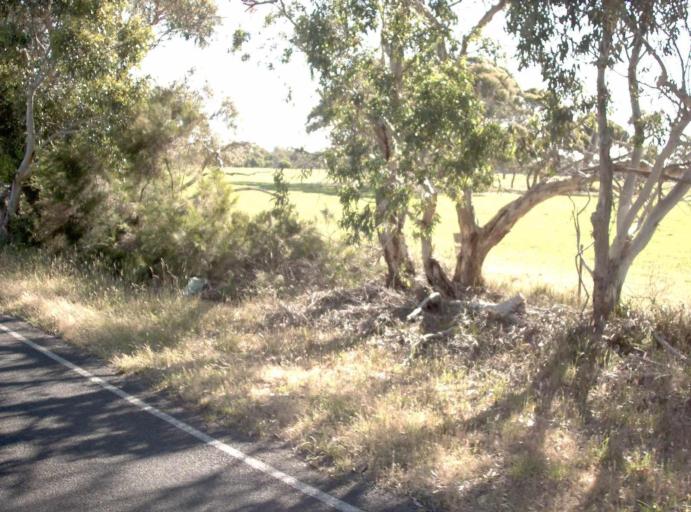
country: AU
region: Victoria
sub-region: Latrobe
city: Morwell
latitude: -38.6987
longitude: 146.3992
